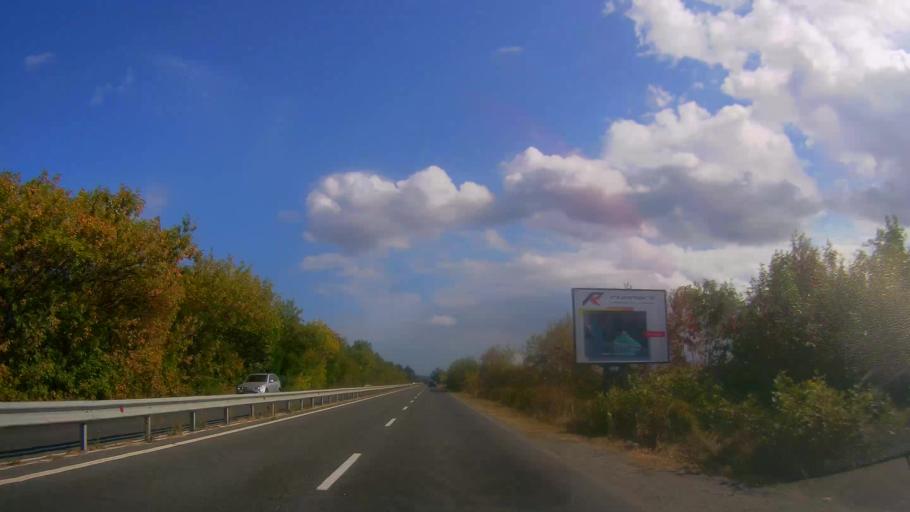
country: BG
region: Burgas
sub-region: Obshtina Sozopol
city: Chernomorets
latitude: 42.4116
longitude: 27.6487
